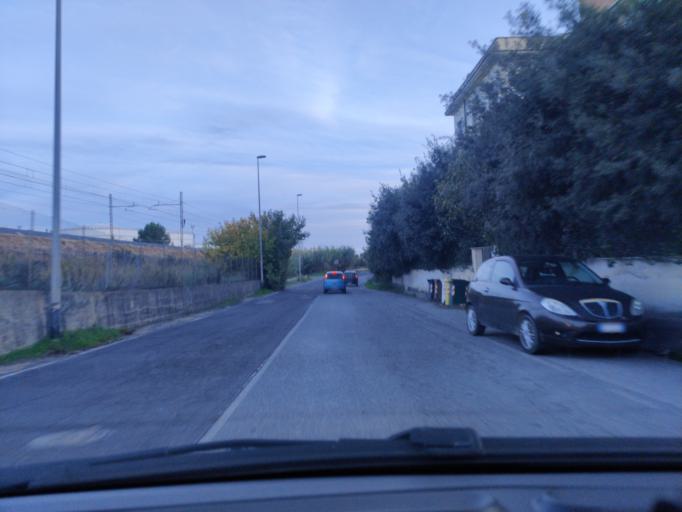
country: IT
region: Latium
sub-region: Citta metropolitana di Roma Capitale
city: Civitavecchia
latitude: 42.1123
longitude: 11.7760
